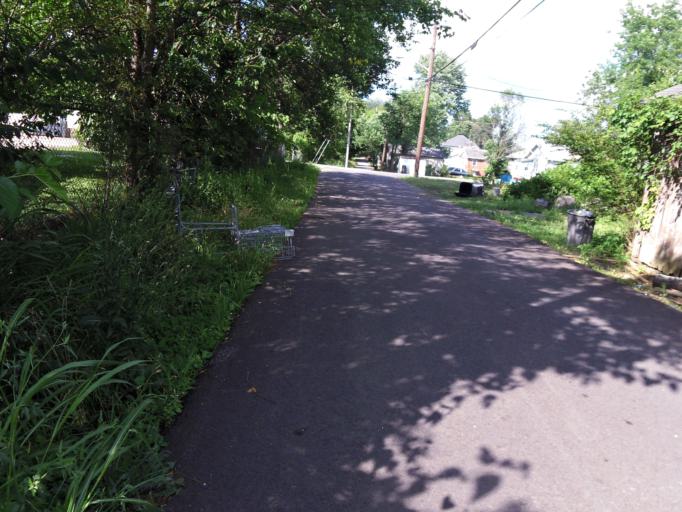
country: US
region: Tennessee
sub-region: Knox County
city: Knoxville
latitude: 35.9953
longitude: -83.9381
